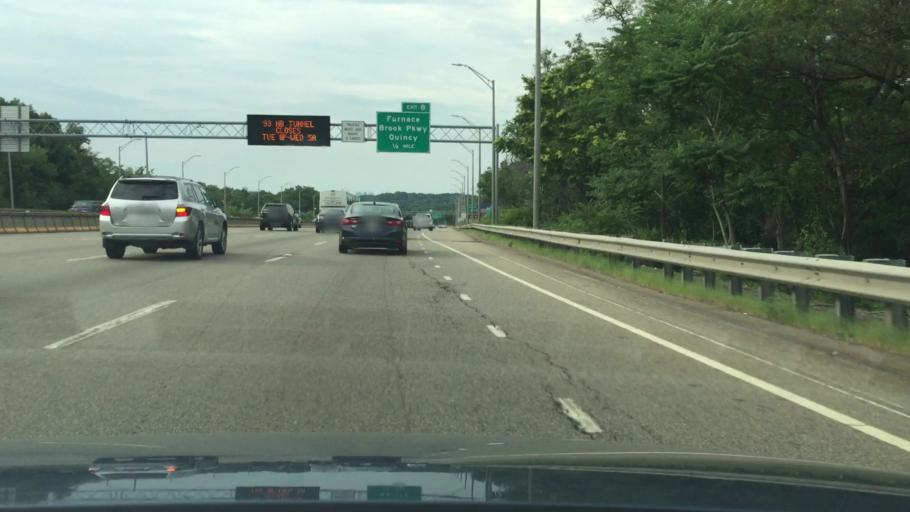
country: US
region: Massachusetts
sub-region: Norfolk County
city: Braintree
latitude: 42.2337
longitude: -71.0229
